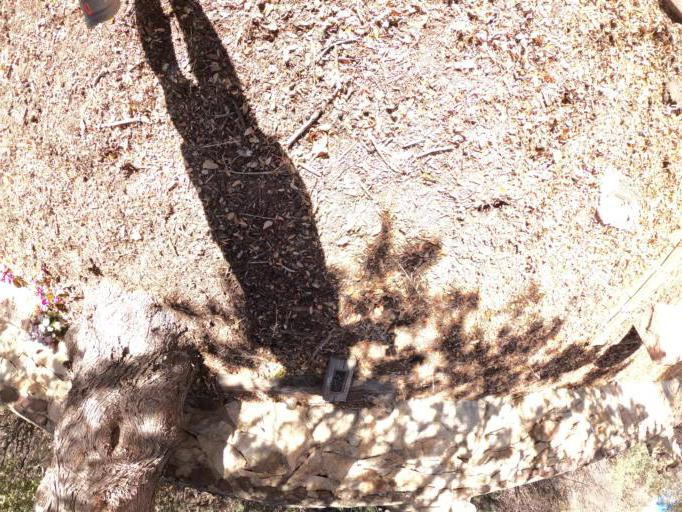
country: US
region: Arizona
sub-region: Yavapai County
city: Verde Village
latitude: 34.5885
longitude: -112.0479
